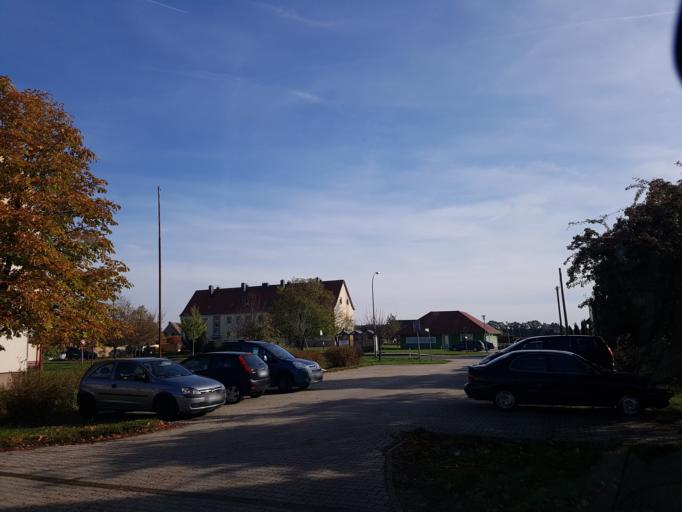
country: DE
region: Brandenburg
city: Elsterwerda
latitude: 51.4251
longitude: 13.4808
